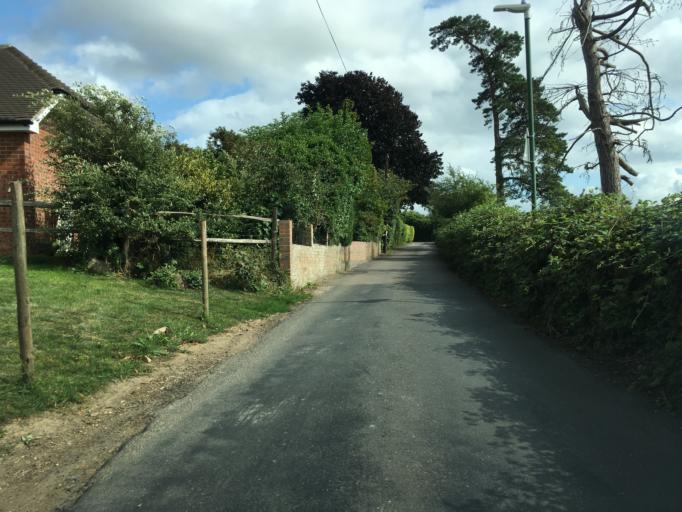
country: GB
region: England
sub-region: Kent
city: Maidstone
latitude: 51.2539
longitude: 0.5199
